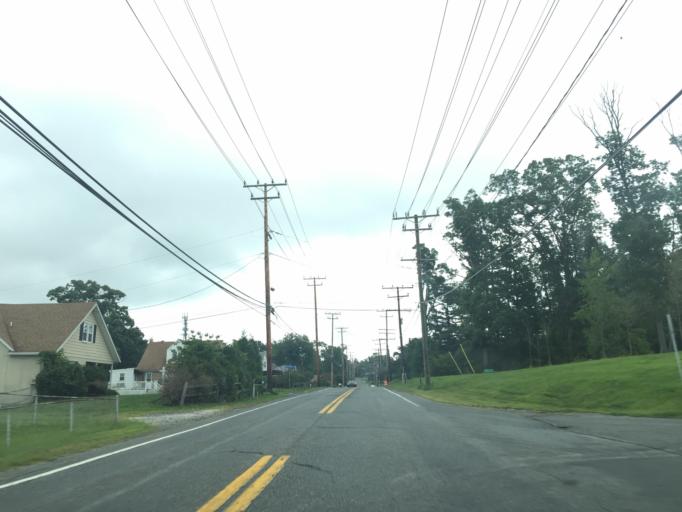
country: US
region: Maryland
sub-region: Harford County
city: Edgewood
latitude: 39.4555
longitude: -76.2849
